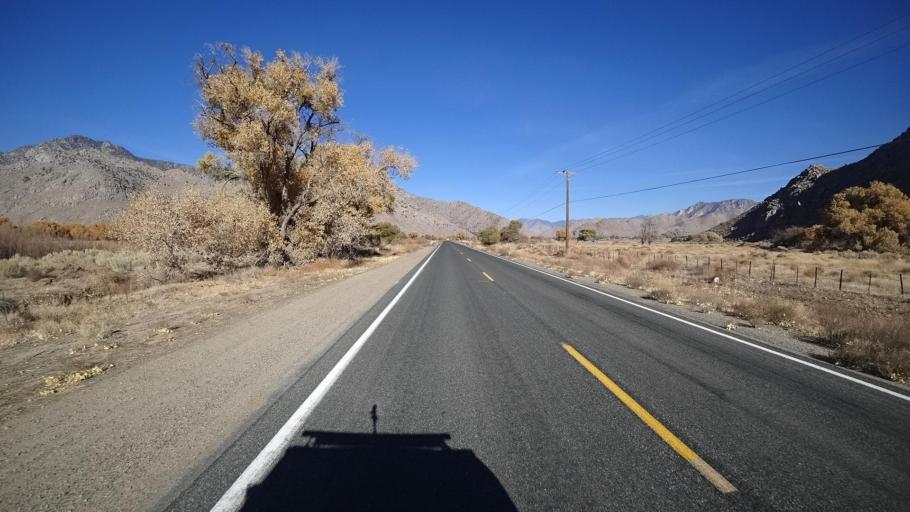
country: US
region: California
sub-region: Kern County
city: Weldon
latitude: 35.6805
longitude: -118.2503
